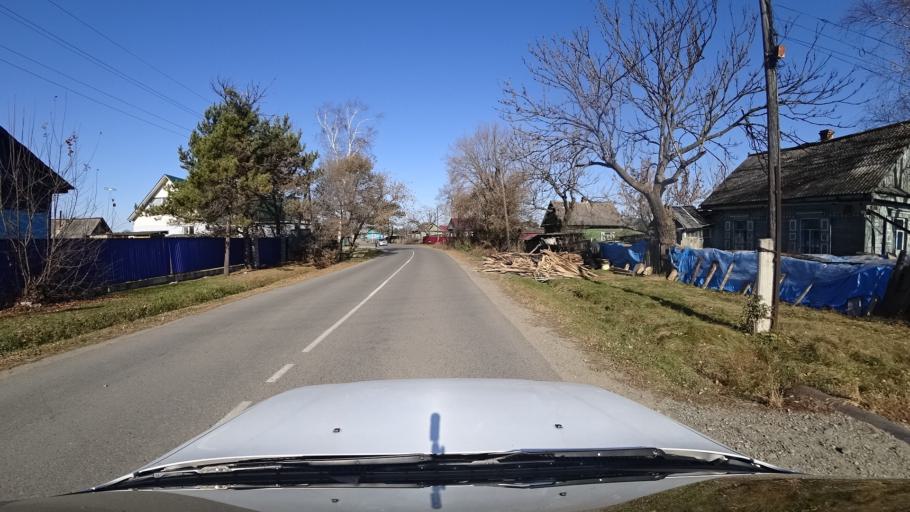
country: RU
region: Primorskiy
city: Dal'nerechensk
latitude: 45.9375
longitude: 133.7031
